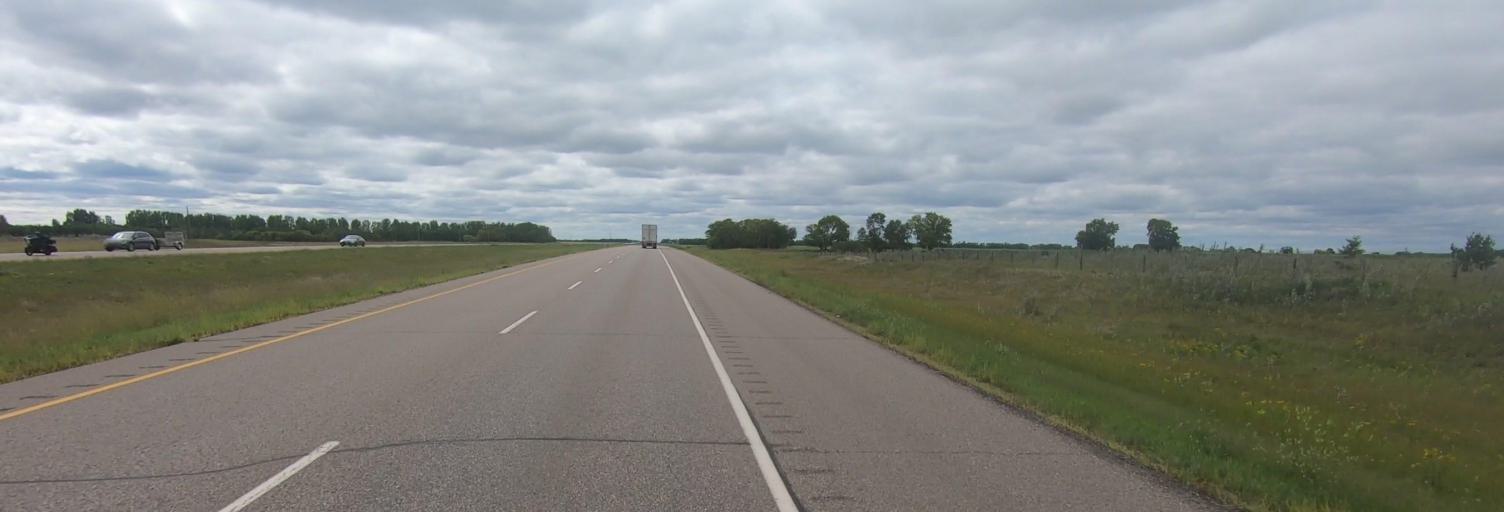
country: CA
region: Manitoba
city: Carberry
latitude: 49.9015
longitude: -99.2787
